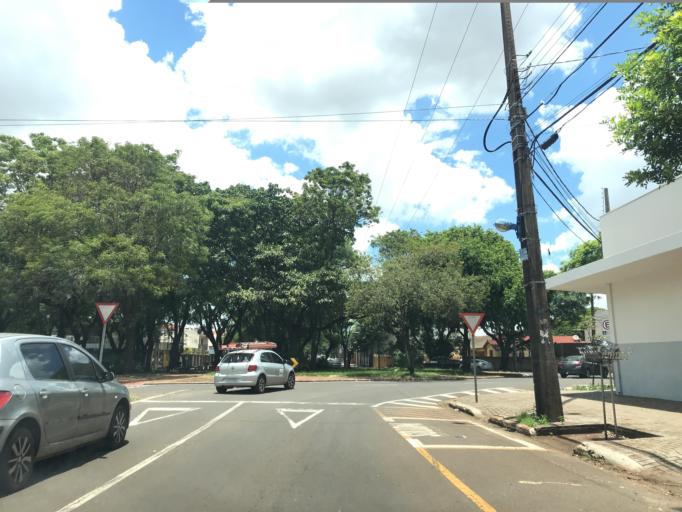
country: BR
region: Parana
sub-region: Maringa
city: Maringa
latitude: -23.3953
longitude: -51.9182
